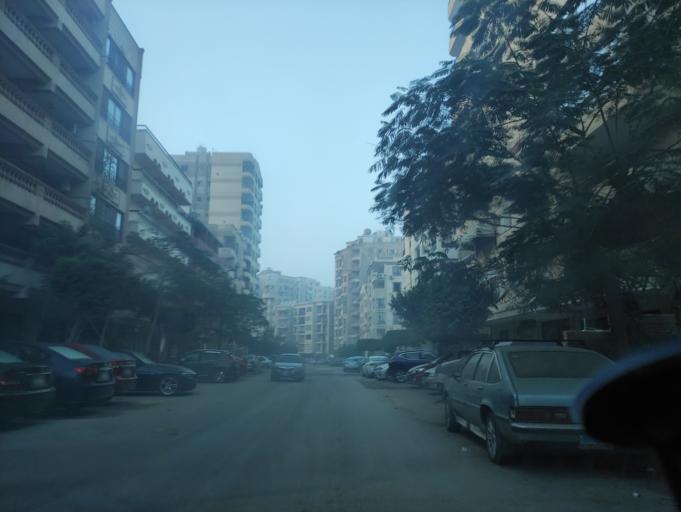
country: EG
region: Muhafazat al Qahirah
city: Cairo
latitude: 30.0501
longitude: 31.3700
